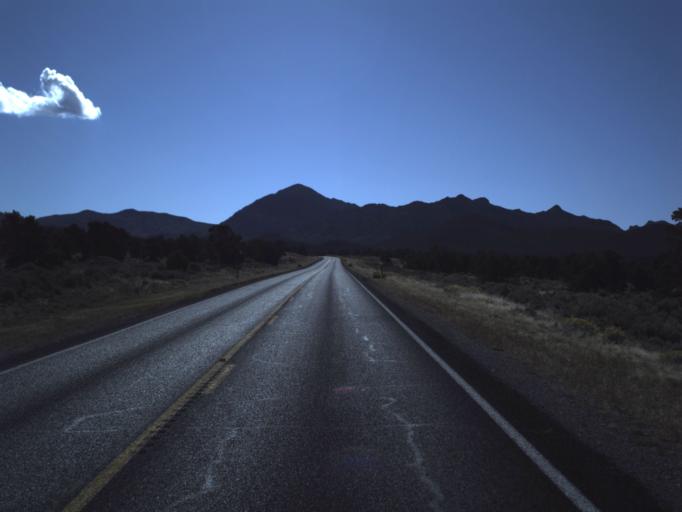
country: US
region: Utah
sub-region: Washington County
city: Enterprise
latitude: 37.6207
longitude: -113.4149
